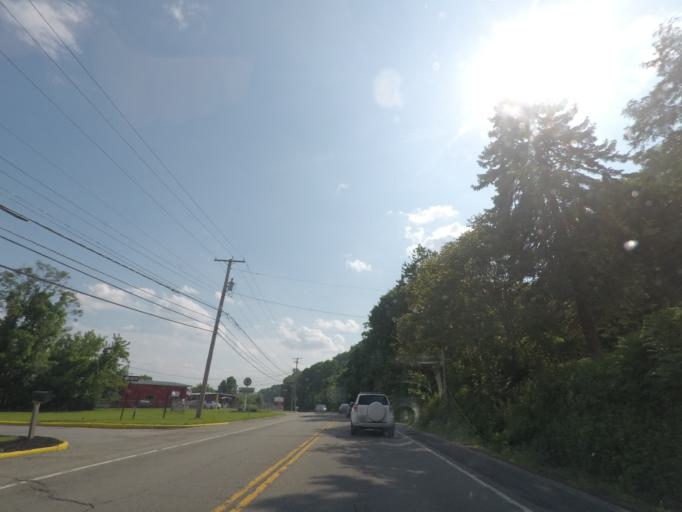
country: US
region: New York
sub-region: Ulster County
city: Marlboro
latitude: 41.5950
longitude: -73.9768
